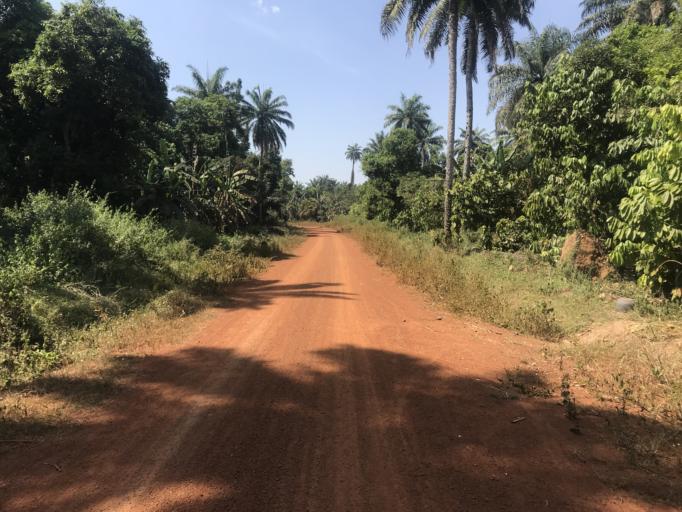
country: NG
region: Osun
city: Ikirun
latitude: 7.9326
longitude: 4.6280
